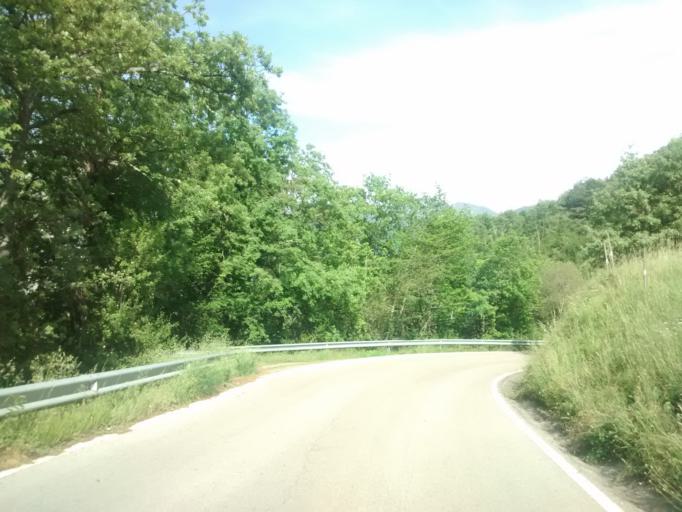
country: ES
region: Cantabria
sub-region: Provincia de Cantabria
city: Potes
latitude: 43.1904
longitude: -4.6170
